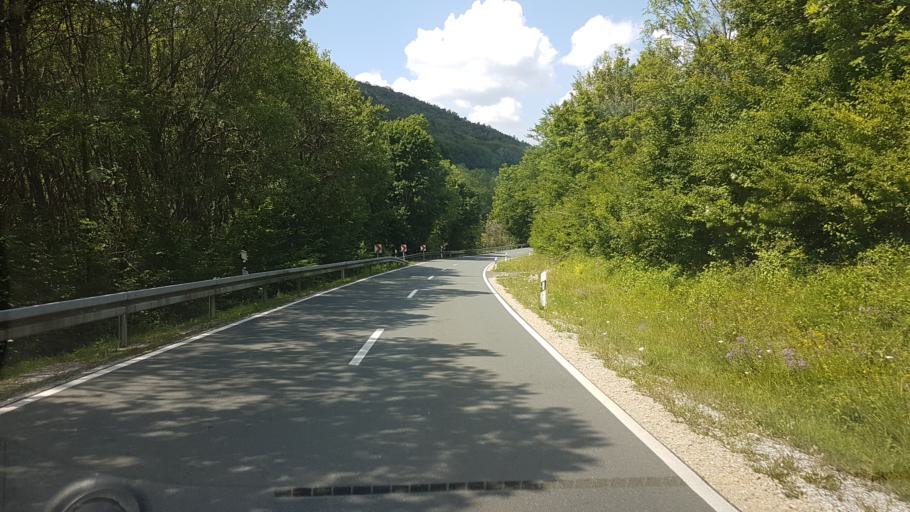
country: DE
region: Bavaria
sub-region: Upper Franconia
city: Egloffstein
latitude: 49.7448
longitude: 11.2429
